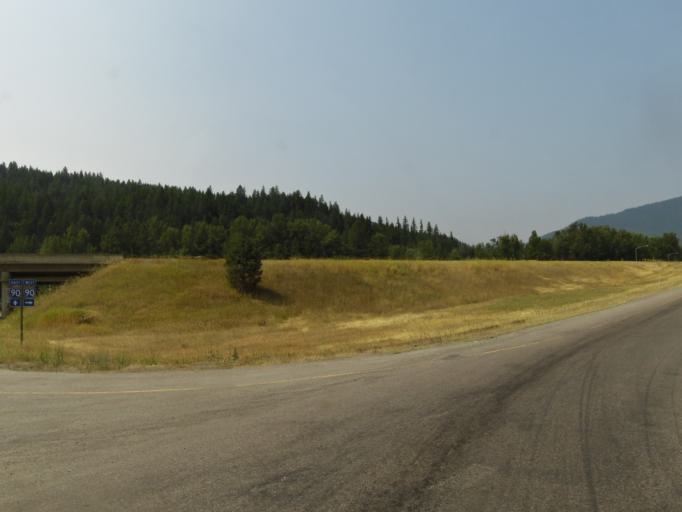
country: US
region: Montana
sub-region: Mineral County
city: Superior
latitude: 47.2971
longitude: -115.0996
